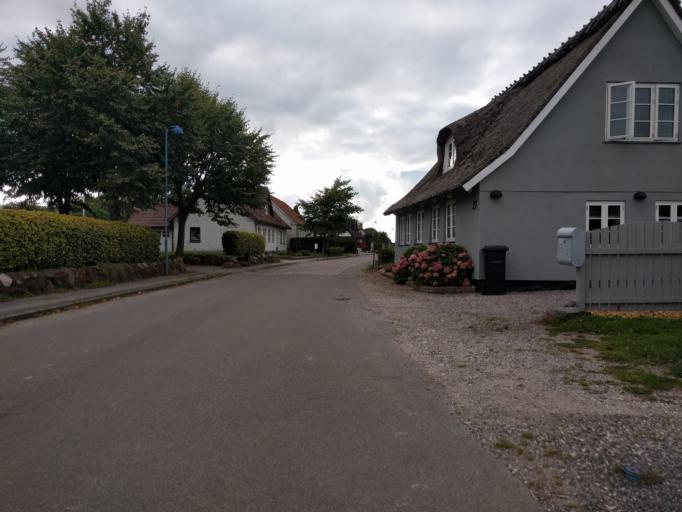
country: DK
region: South Denmark
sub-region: Kerteminde Kommune
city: Munkebo
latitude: 55.4506
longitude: 10.5277
